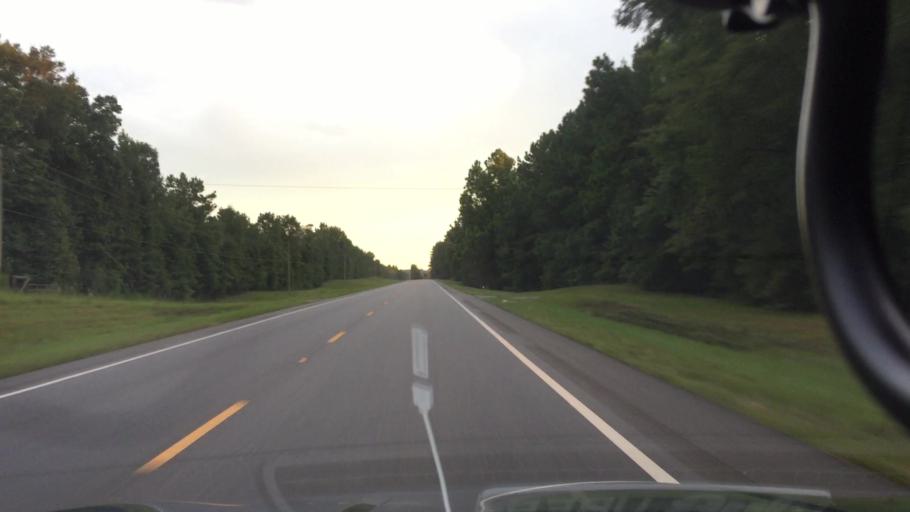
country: US
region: Alabama
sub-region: Coffee County
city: New Brockton
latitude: 31.5030
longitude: -85.9155
